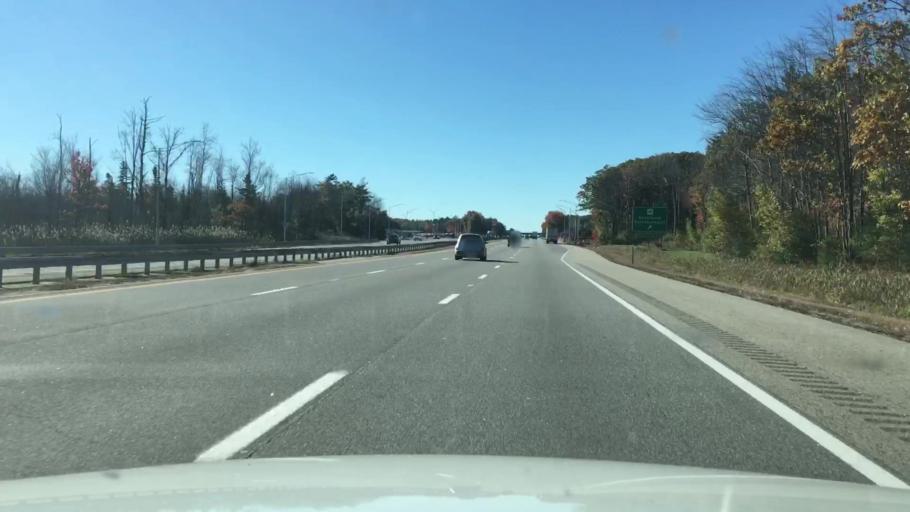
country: US
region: Maine
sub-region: York County
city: West Kennebunk
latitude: 43.4158
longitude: -70.5567
